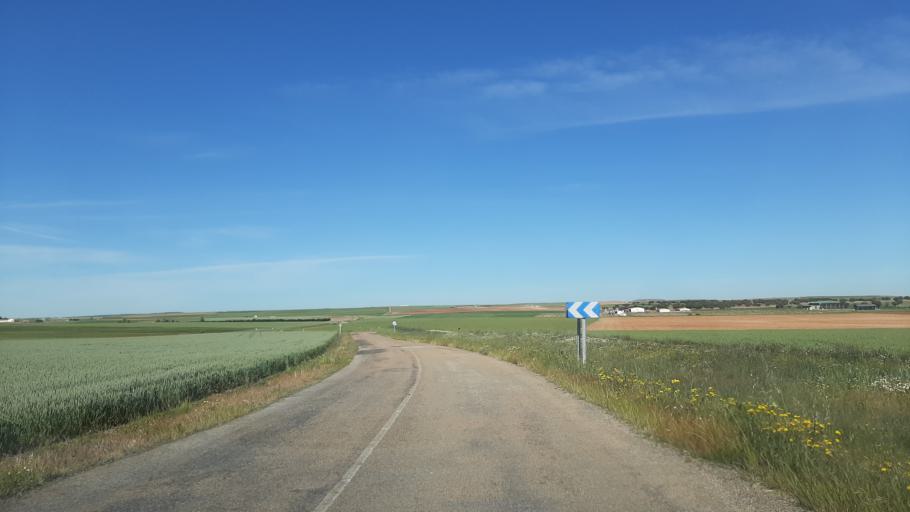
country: ES
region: Castille and Leon
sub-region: Provincia de Salamanca
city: Aldeaseca de Alba
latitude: 40.8251
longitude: -5.4273
